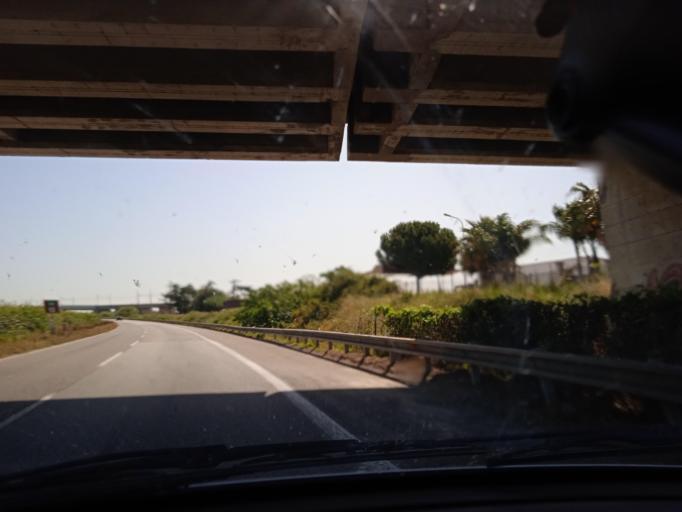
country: IT
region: Sicily
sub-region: Messina
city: Barcellona Pozzo di Gotto
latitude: 38.1645
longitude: 15.2101
